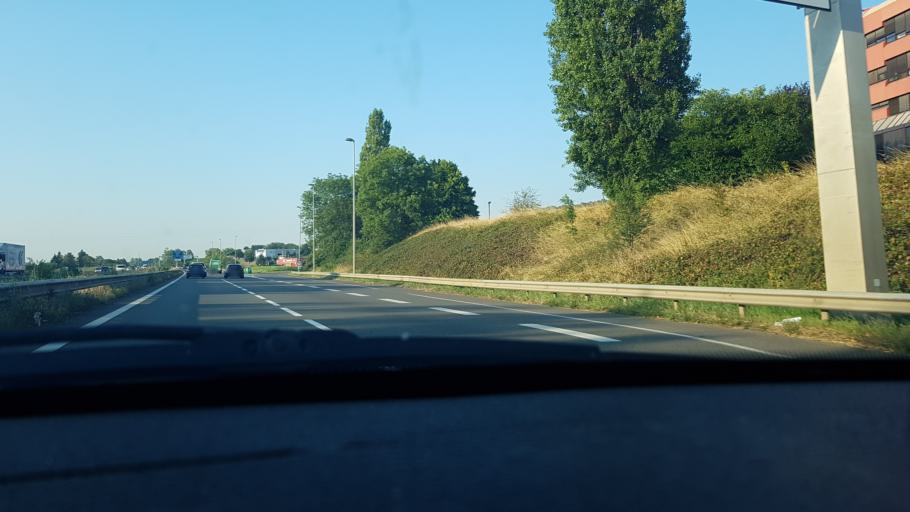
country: FR
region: Lorraine
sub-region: Departement de Meurthe-et-Moselle
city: Vandoeuvre-les-Nancy
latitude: 48.6431
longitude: 6.1811
